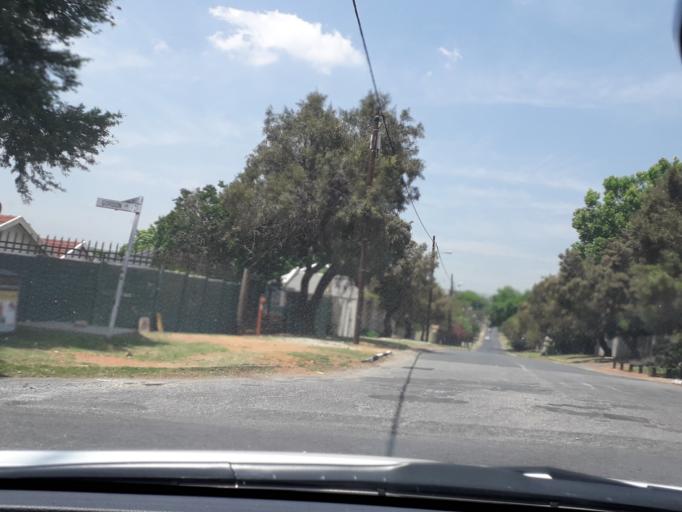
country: ZA
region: Gauteng
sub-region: City of Johannesburg Metropolitan Municipality
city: Johannesburg
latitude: -26.1100
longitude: 28.0077
